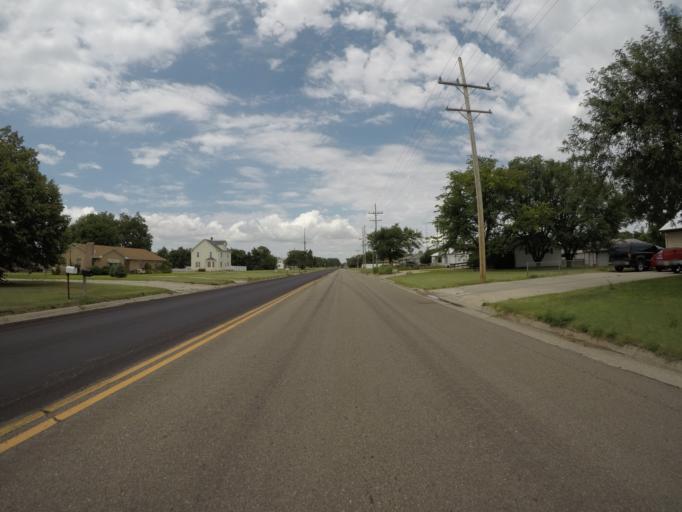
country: US
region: Kansas
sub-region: Rawlins County
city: Atwood
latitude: 39.8019
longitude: -101.0469
